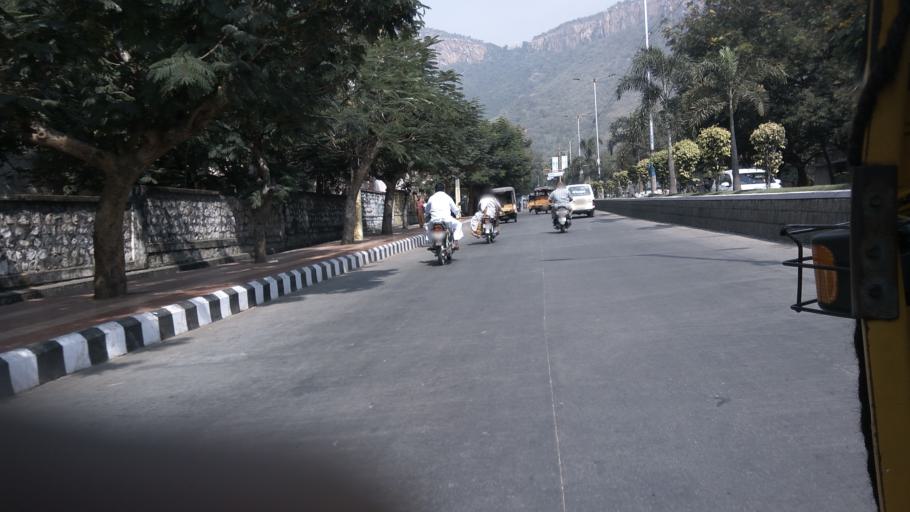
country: IN
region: Andhra Pradesh
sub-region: Chittoor
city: Akkarampalle
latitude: 13.6437
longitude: 79.4081
